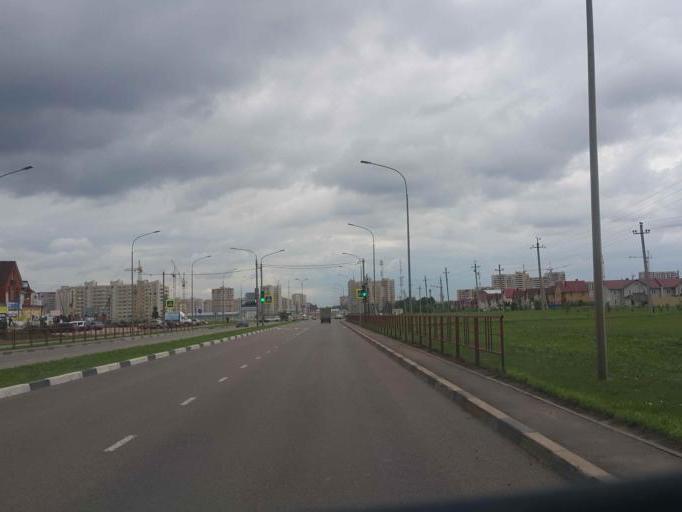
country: RU
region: Tambov
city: Tambov
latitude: 52.7726
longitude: 41.3866
